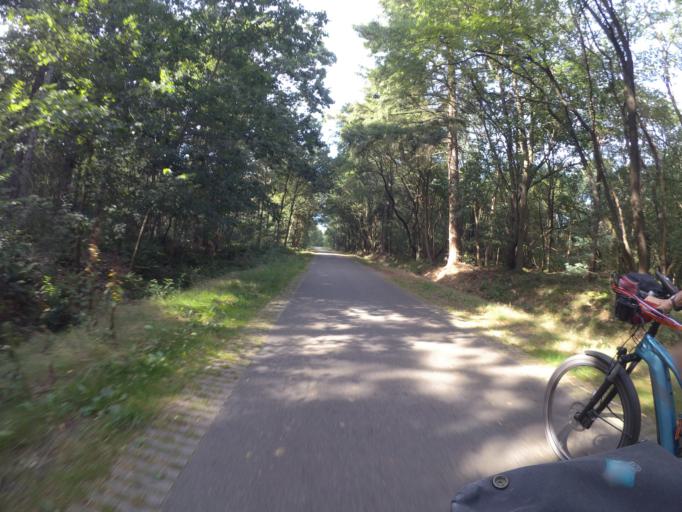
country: NL
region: Overijssel
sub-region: Gemeente Dalfsen
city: Dalfsen
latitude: 52.5477
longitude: 6.3665
